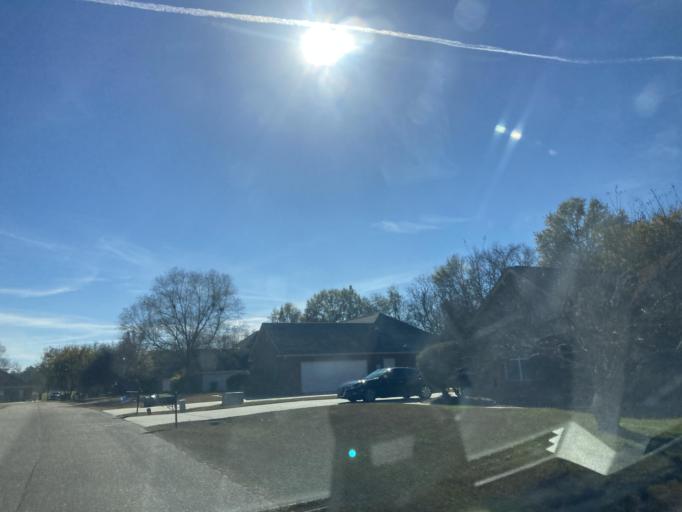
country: US
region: Mississippi
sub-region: Forrest County
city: Petal
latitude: 31.3180
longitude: -89.1876
